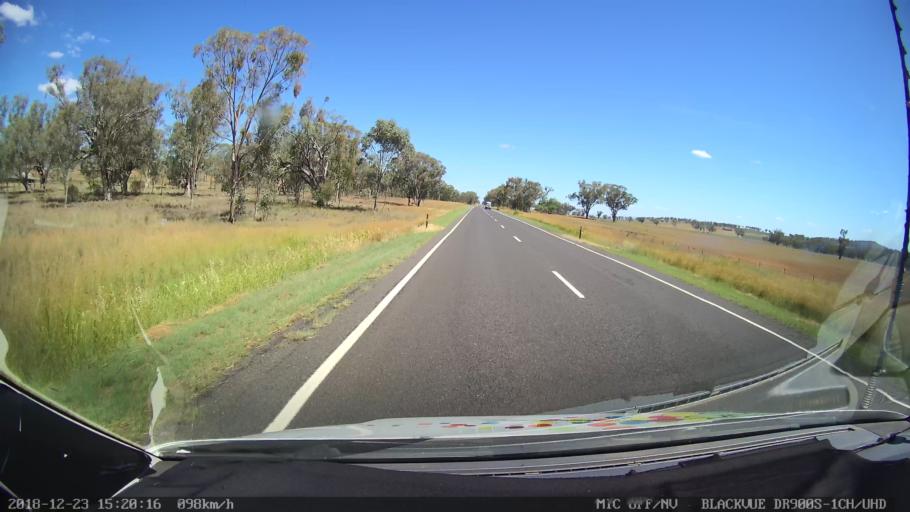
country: AU
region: New South Wales
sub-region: Tamworth Municipality
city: Manilla
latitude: -30.8404
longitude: 150.7886
